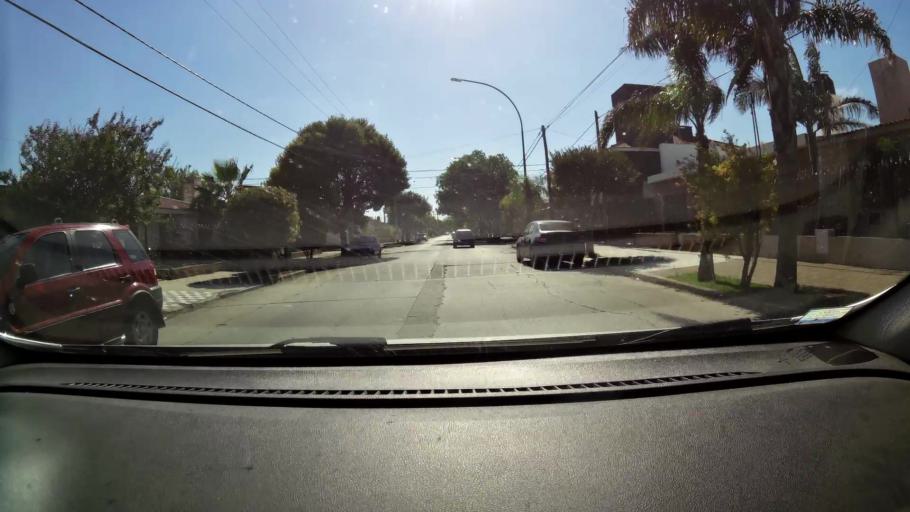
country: AR
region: Cordoba
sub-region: Departamento de Capital
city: Cordoba
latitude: -31.3700
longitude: -64.1775
